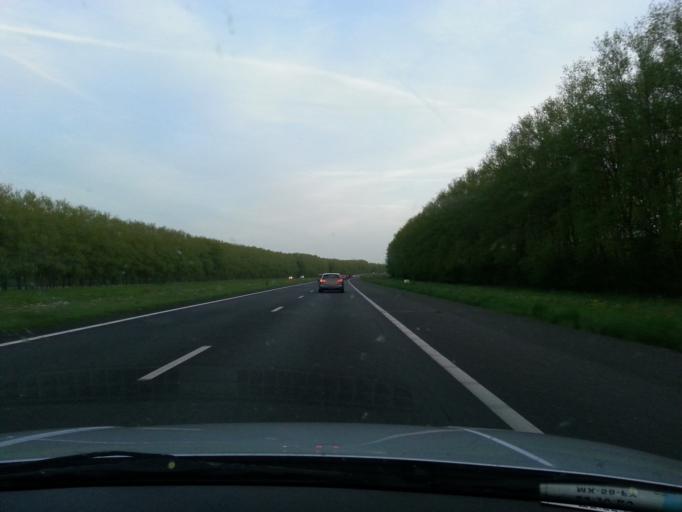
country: NL
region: Flevoland
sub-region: Gemeente Lelystad
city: Lelystad
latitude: 52.5129
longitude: 5.5331
